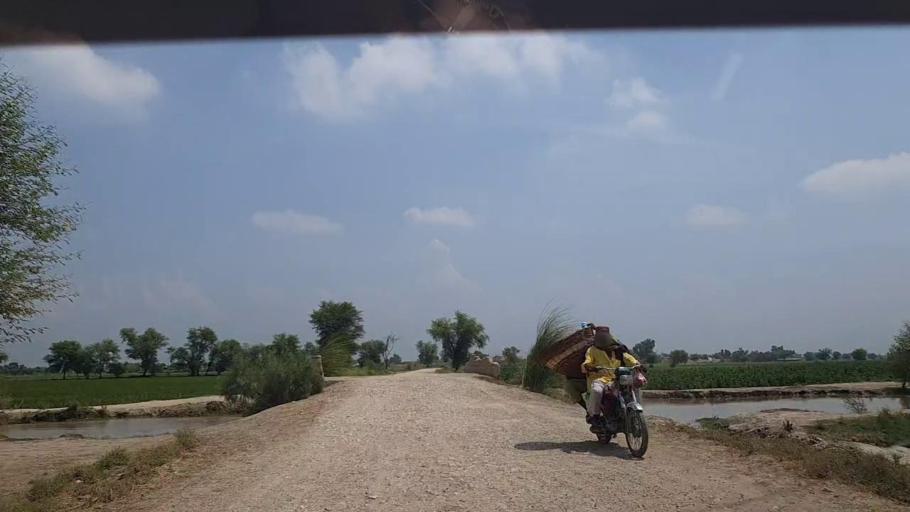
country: PK
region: Sindh
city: Khanpur
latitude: 27.8907
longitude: 69.4033
